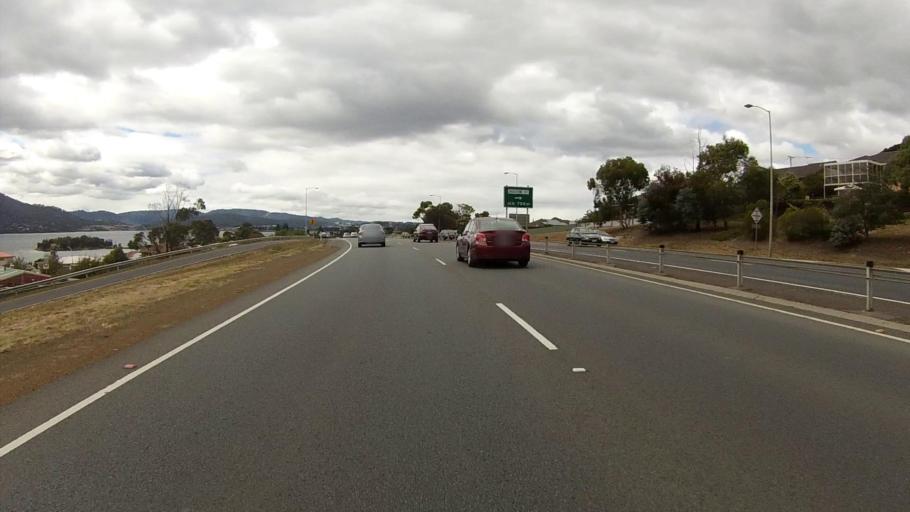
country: AU
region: Tasmania
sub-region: Glenorchy
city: Berriedale
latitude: -42.8154
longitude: 147.2533
